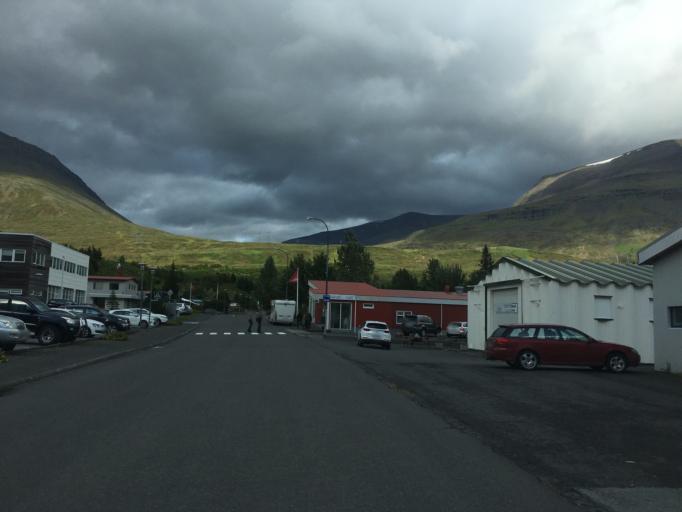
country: IS
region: East
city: Reydarfjoerdur
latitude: 65.0318
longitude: -14.2187
